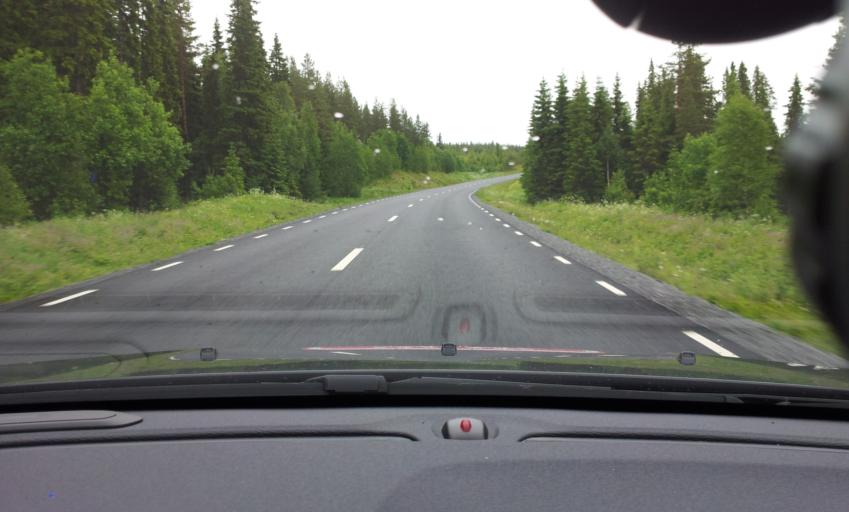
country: SE
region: Jaemtland
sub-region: Stroemsunds Kommun
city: Stroemsund
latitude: 63.6635
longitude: 15.1426
